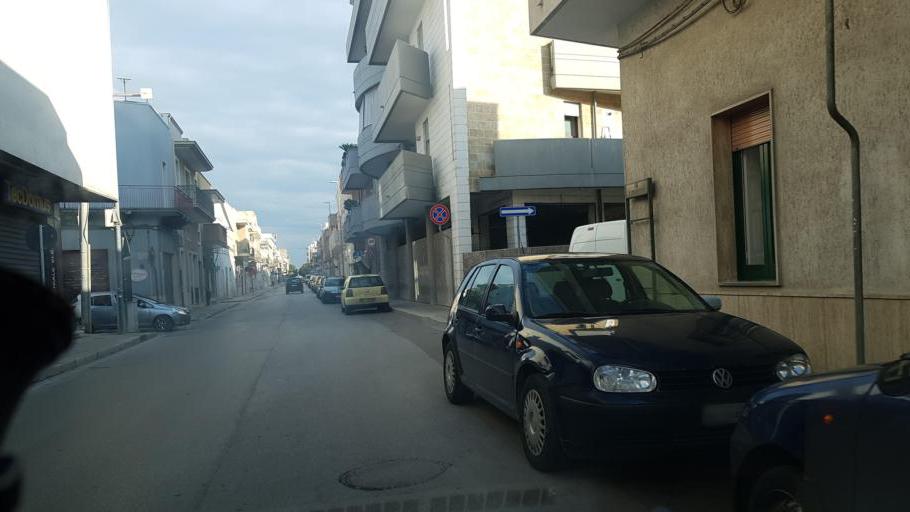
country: IT
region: Apulia
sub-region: Provincia di Brindisi
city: Francavilla Fontana
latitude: 40.5284
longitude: 17.5776
